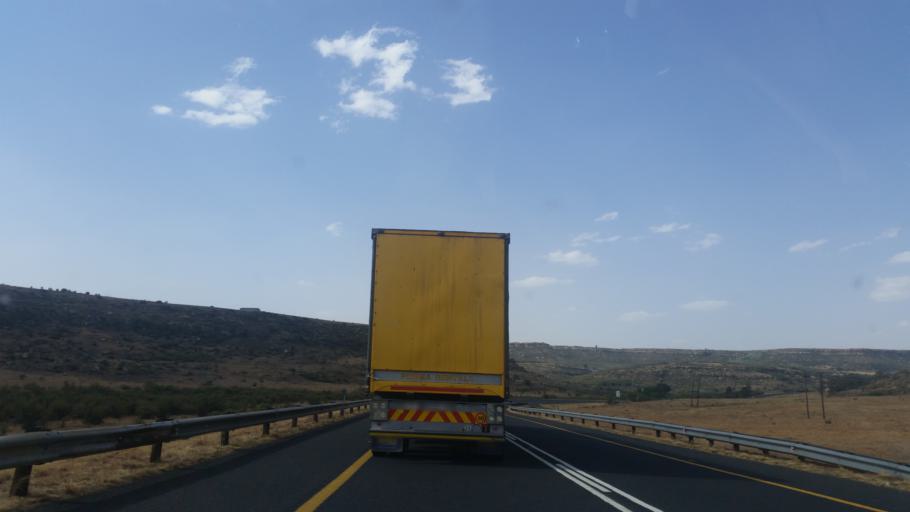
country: ZA
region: Orange Free State
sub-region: Thabo Mofutsanyana District Municipality
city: Bethlehem
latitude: -28.3015
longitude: 28.5057
